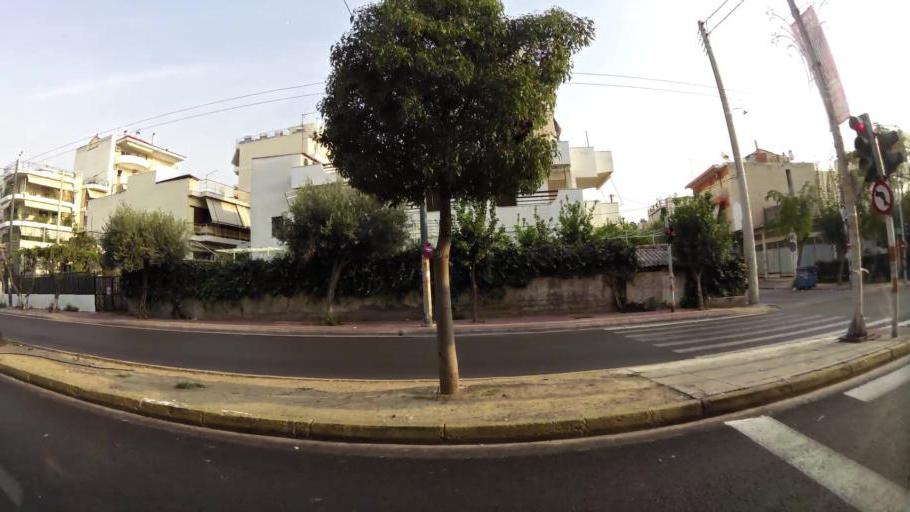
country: GR
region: Attica
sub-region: Nomarchia Athinas
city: Petroupolis
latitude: 38.0363
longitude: 23.6882
